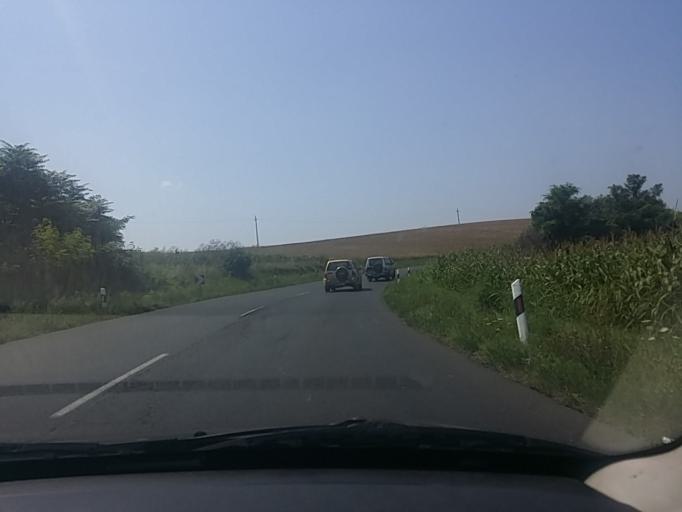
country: HU
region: Tolna
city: Tamasi
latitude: 46.5823
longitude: 18.2080
